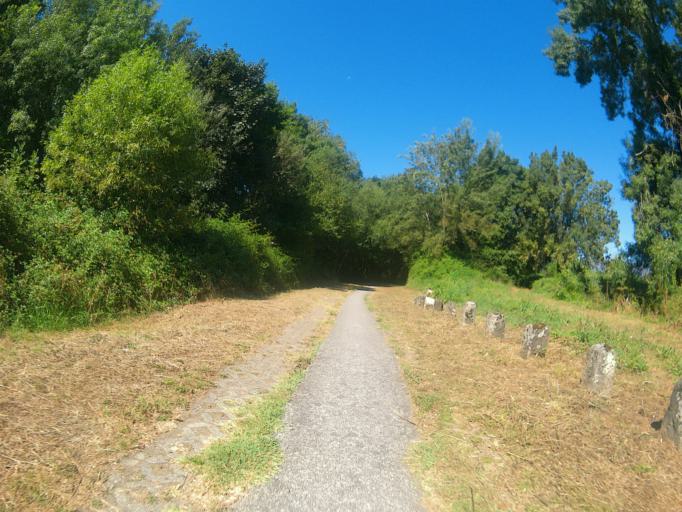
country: PT
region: Viana do Castelo
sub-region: Ponte de Lima
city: Ponte de Lima
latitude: 41.7634
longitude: -8.6012
